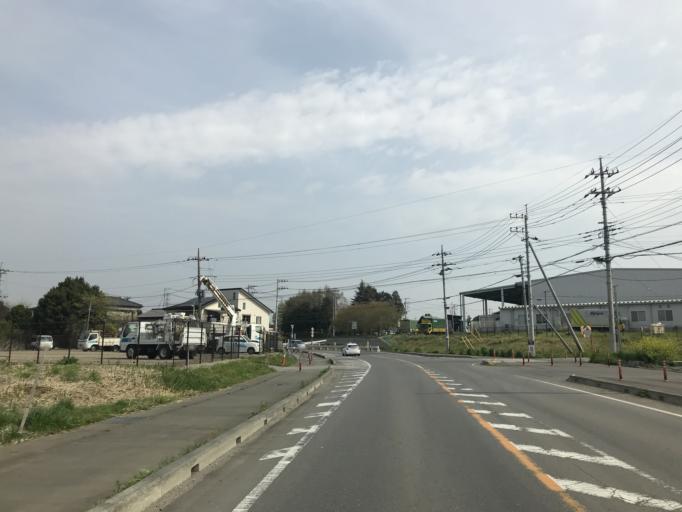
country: JP
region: Ibaraki
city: Moriya
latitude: 35.9677
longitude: 139.9902
